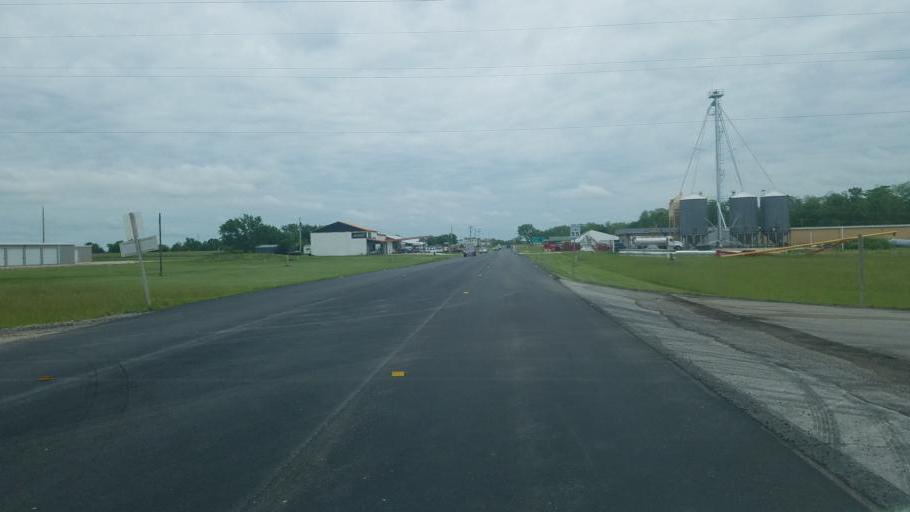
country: US
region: Missouri
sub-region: Morgan County
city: Versailles
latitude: 38.4453
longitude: -92.8281
